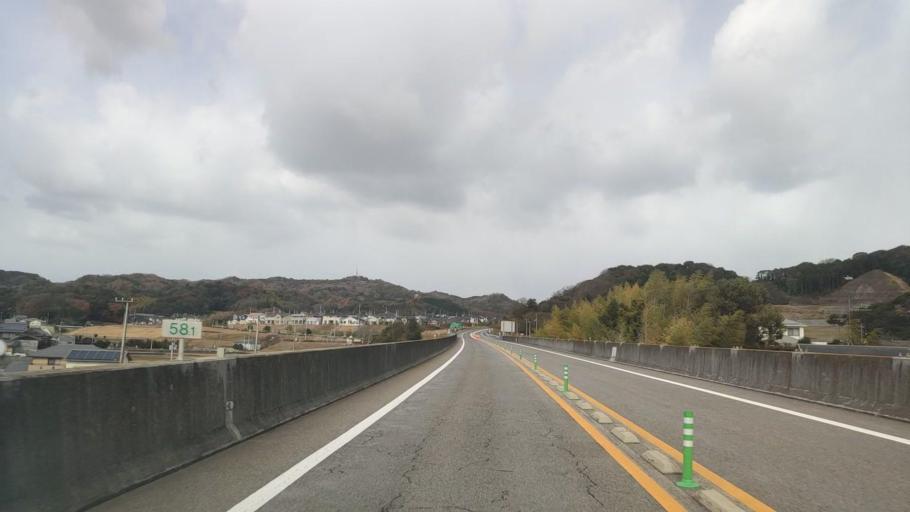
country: JP
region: Ehime
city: Hojo
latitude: 34.0633
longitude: 132.9731
